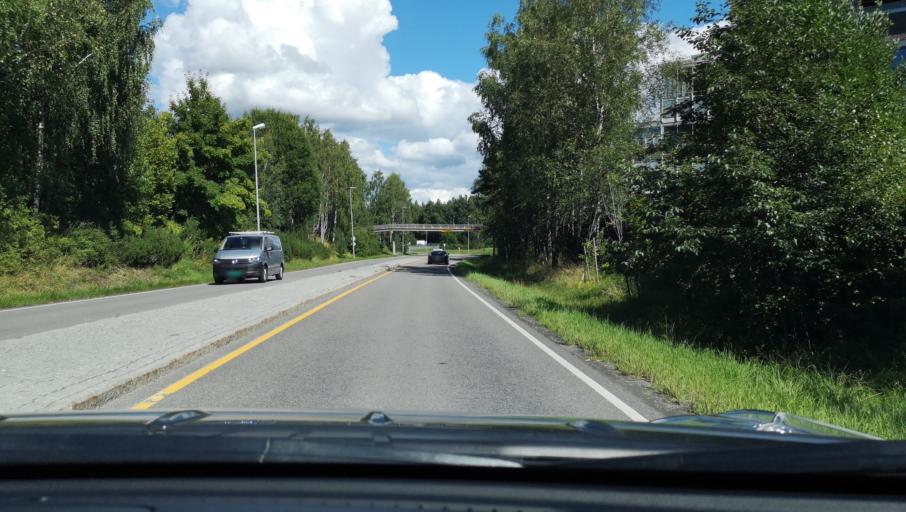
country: NO
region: Akershus
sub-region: As
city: As
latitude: 59.6651
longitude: 10.7889
